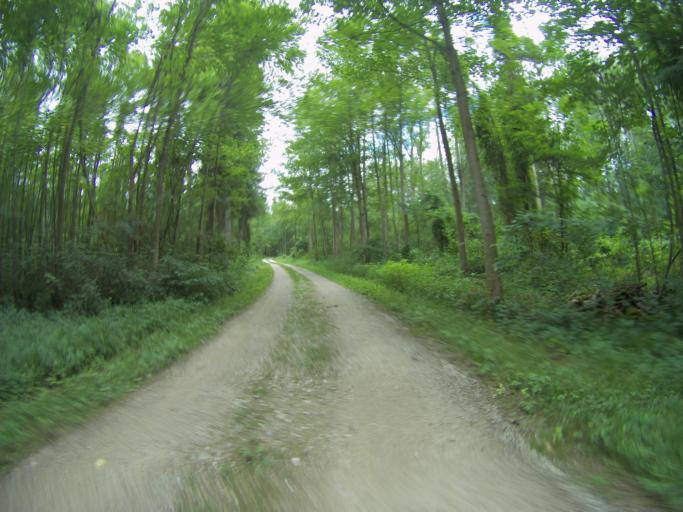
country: DE
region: Bavaria
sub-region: Upper Bavaria
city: Freising
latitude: 48.3700
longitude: 11.7380
